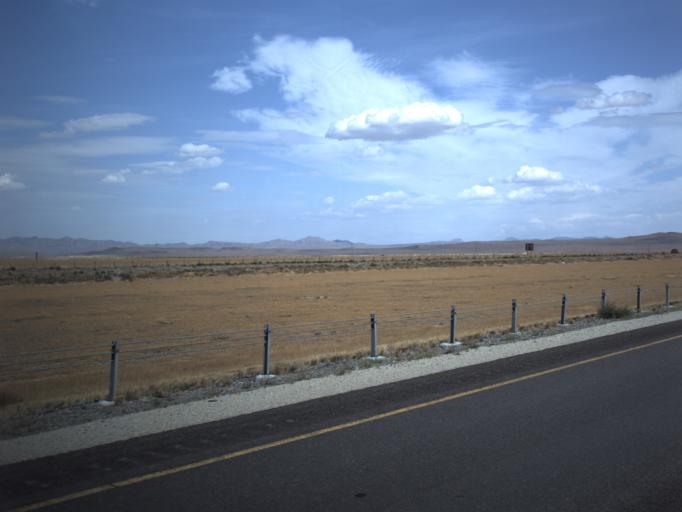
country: US
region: Utah
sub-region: Tooele County
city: Grantsville
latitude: 40.7263
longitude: -113.2458
